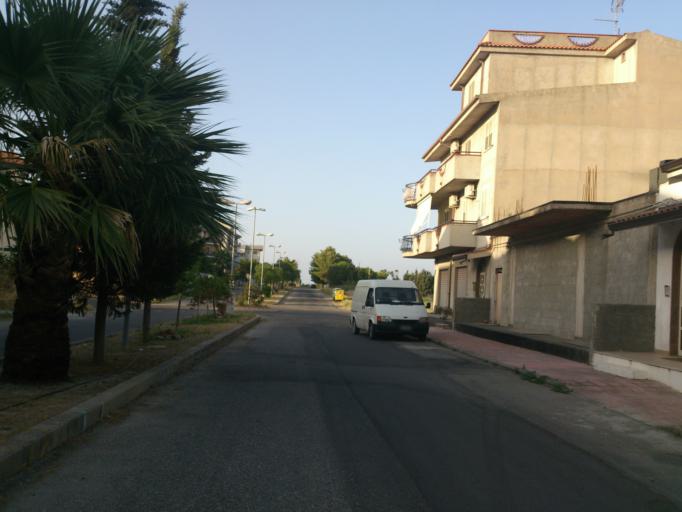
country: IT
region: Calabria
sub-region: Provincia di Reggio Calabria
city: Monasterace Marina
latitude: 38.4381
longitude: 16.5731
